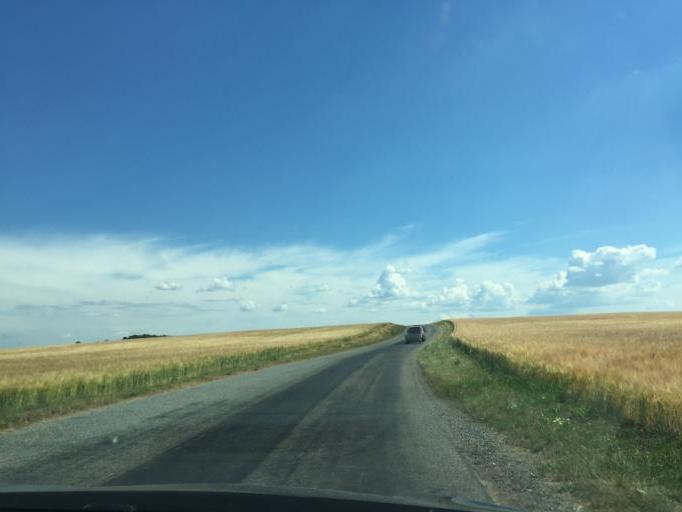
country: DK
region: South Denmark
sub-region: Odense Kommune
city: Bellinge
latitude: 55.2492
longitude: 10.2825
